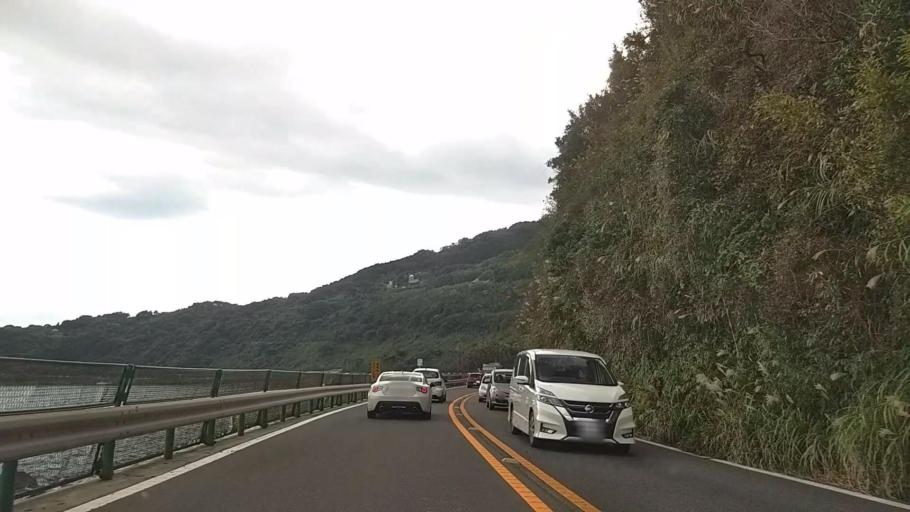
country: JP
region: Kanagawa
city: Odawara
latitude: 35.1873
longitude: 139.1392
